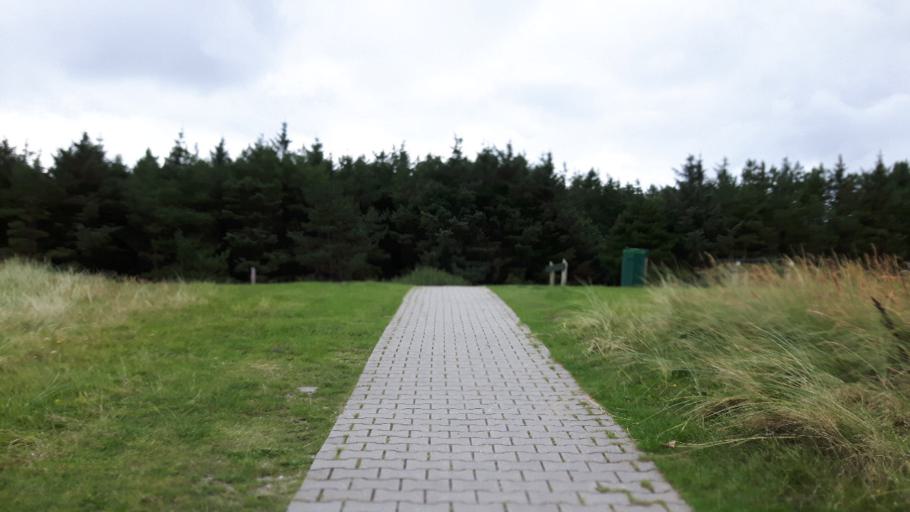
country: NL
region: Friesland
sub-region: Gemeente Ameland
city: Nes
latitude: 53.4531
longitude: 5.7149
